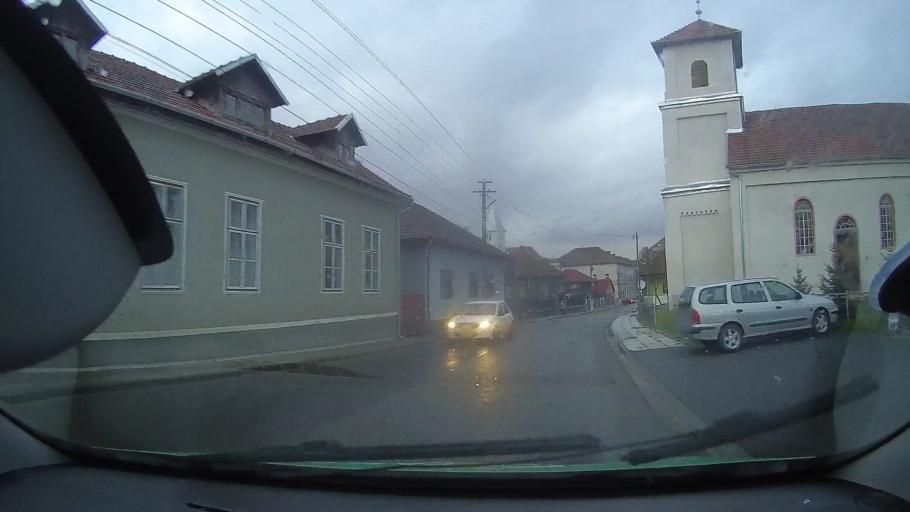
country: RO
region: Hunedoara
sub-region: Comuna Baia de Cris
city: Baia de Cris
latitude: 46.1746
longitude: 22.7155
